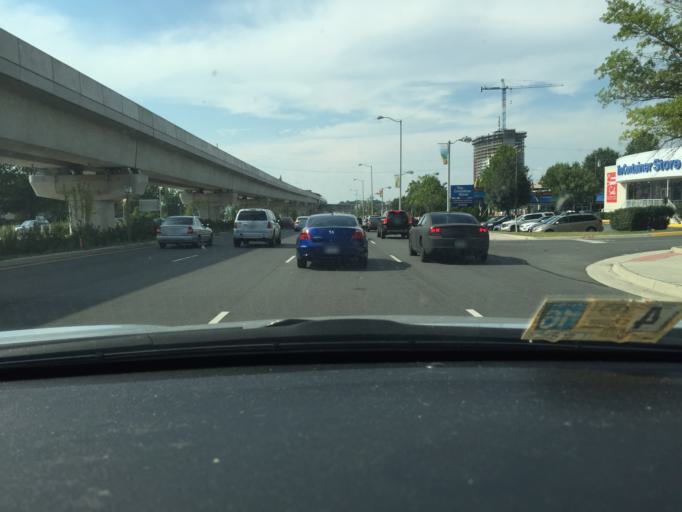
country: US
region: Virginia
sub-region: Fairfax County
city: Tysons Corner
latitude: 38.9260
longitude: -77.2384
